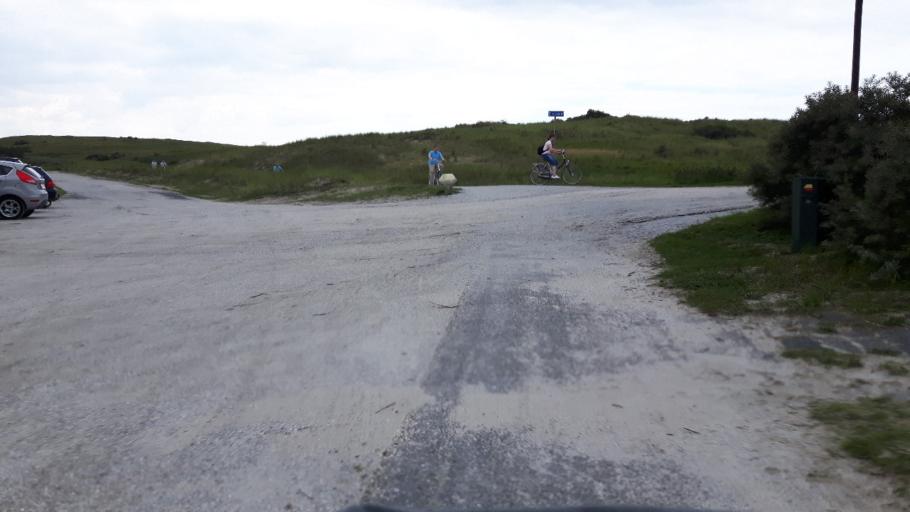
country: NL
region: Friesland
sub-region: Gemeente Ameland
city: Nes
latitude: 53.4609
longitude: 5.8347
